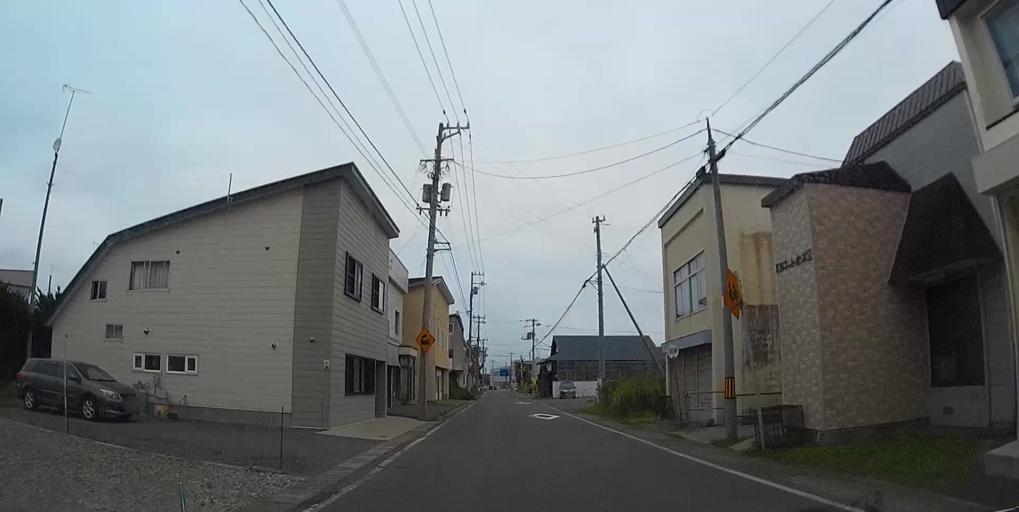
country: JP
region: Hokkaido
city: Nanae
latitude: 42.2561
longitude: 140.2664
